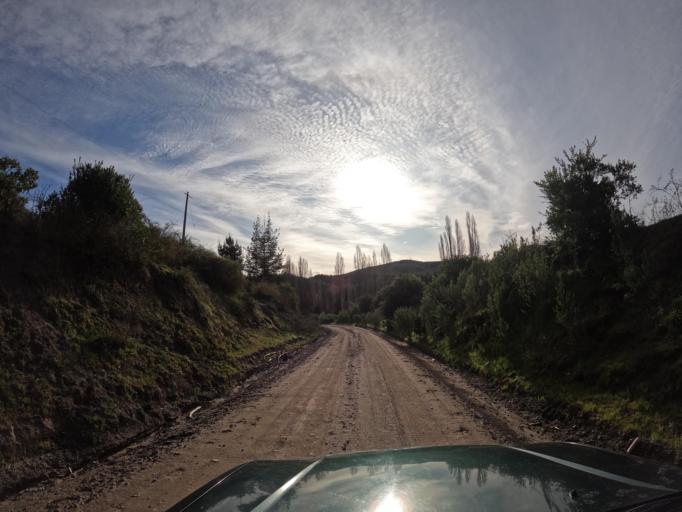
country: CL
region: Biobio
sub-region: Provincia de Biobio
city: La Laja
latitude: -37.1945
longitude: -72.7601
